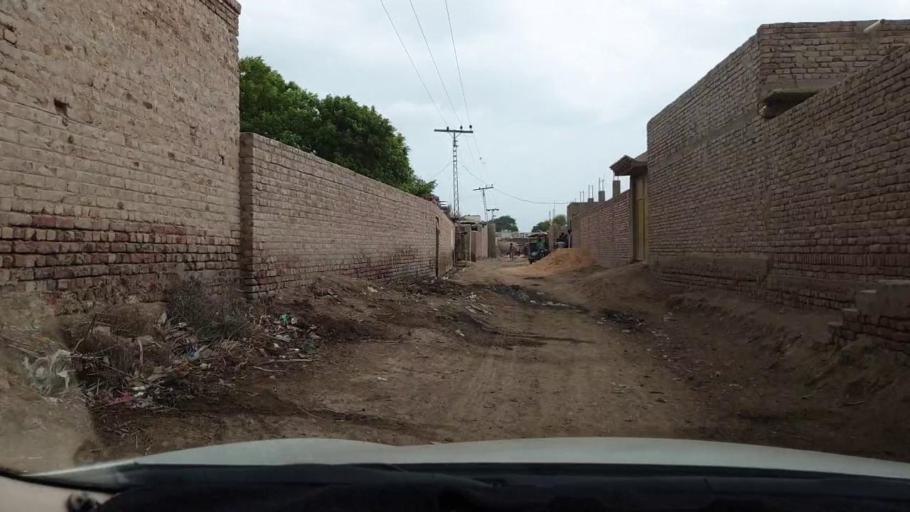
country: PK
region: Sindh
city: Tando Muhammad Khan
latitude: 25.1106
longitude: 68.6088
